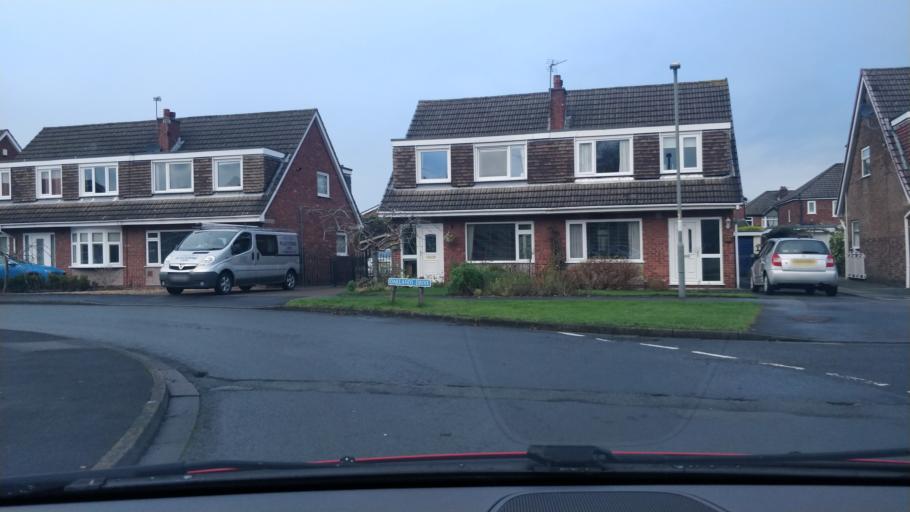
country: GB
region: England
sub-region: Lancashire
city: Preston
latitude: 53.7428
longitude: -2.7360
